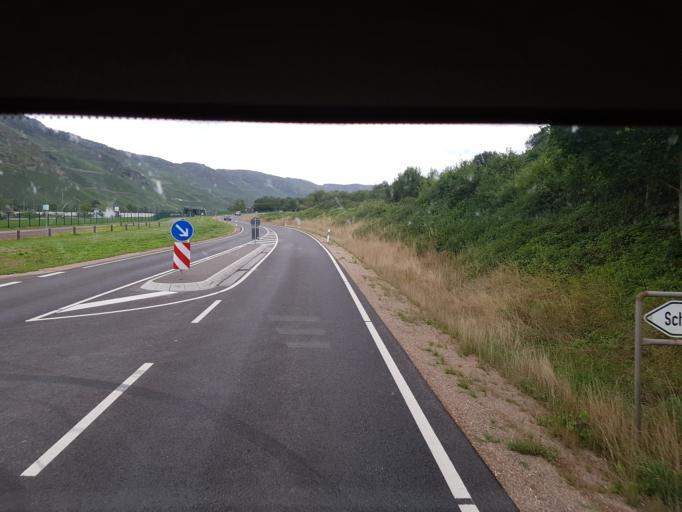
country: DE
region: Rheinland-Pfalz
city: Zeltingen-Rachtig
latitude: 49.9486
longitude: 7.0199
